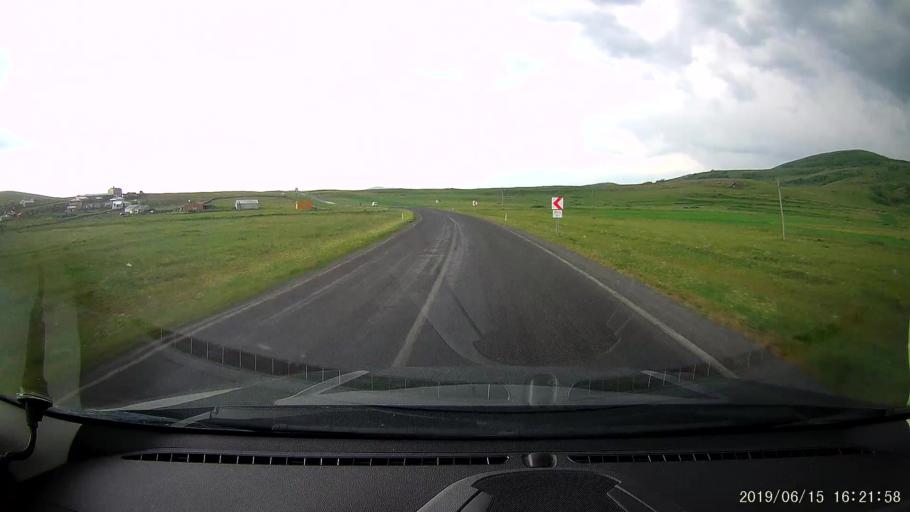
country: TR
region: Ardahan
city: Hanak
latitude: 41.1928
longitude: 42.8459
